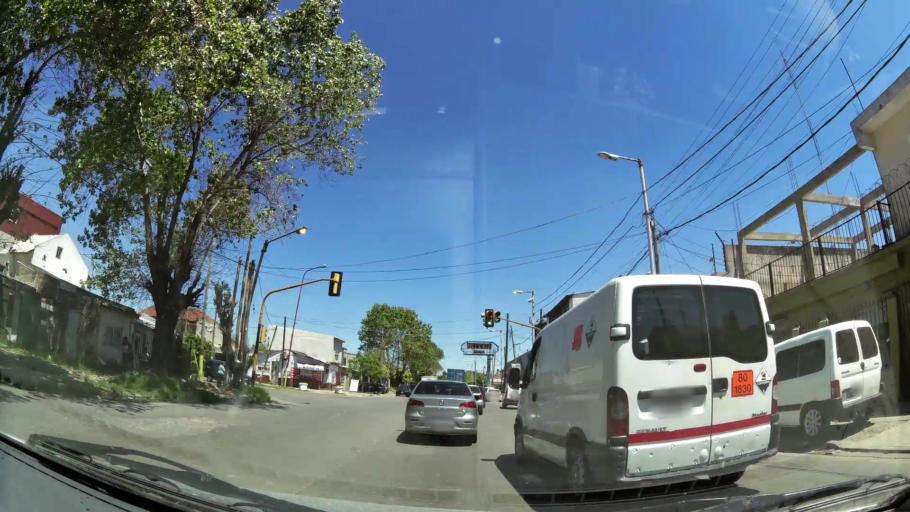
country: AR
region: Buenos Aires
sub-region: Partido de Quilmes
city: Quilmes
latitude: -34.7166
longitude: -58.3224
